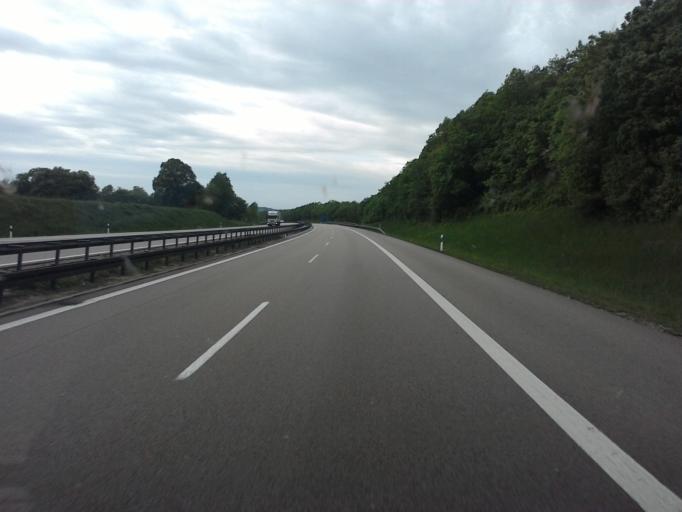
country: DE
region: Bavaria
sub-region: Upper Palatinate
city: Velburg
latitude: 49.2382
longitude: 11.6363
